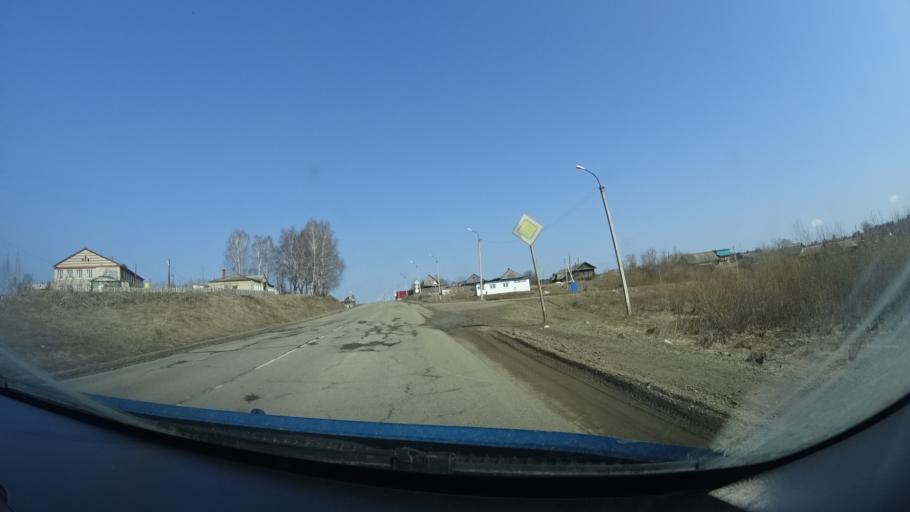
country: RU
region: Perm
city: Yugo-Kamskiy
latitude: 57.4524
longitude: 55.6565
